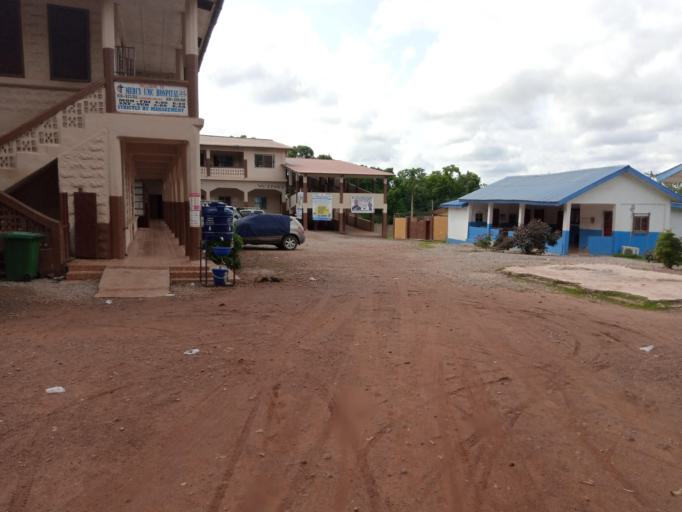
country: SL
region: Southern Province
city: Bo
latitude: 7.9766
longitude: -11.7376
